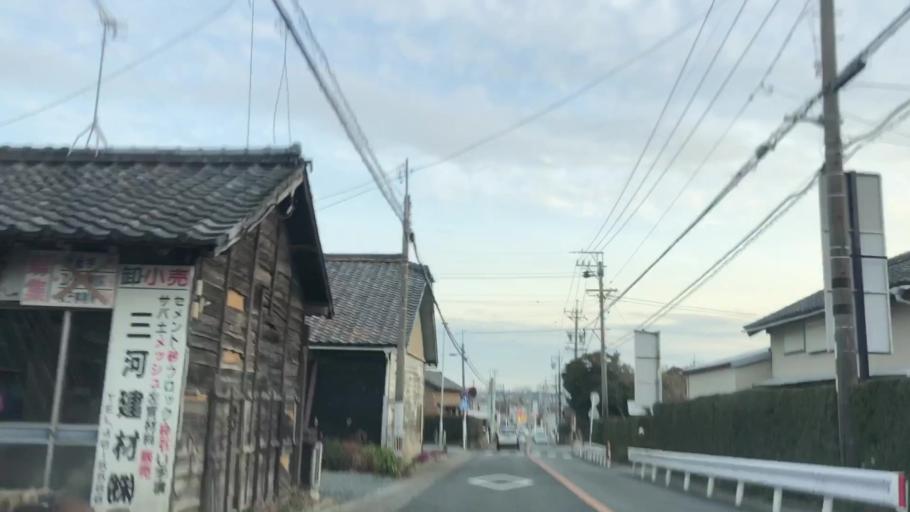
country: JP
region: Aichi
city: Toyohashi
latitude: 34.7210
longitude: 137.4041
